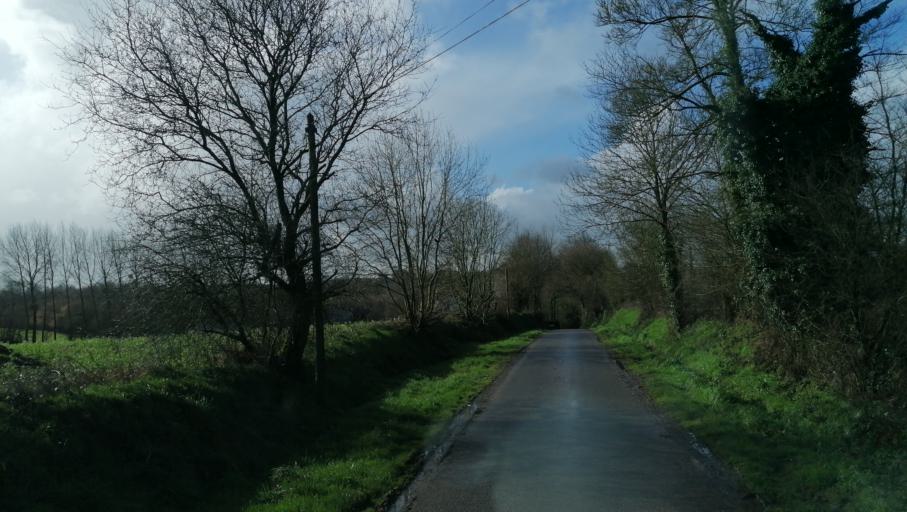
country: FR
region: Brittany
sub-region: Departement des Cotes-d'Armor
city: Lanrodec
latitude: 48.4975
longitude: -3.0163
